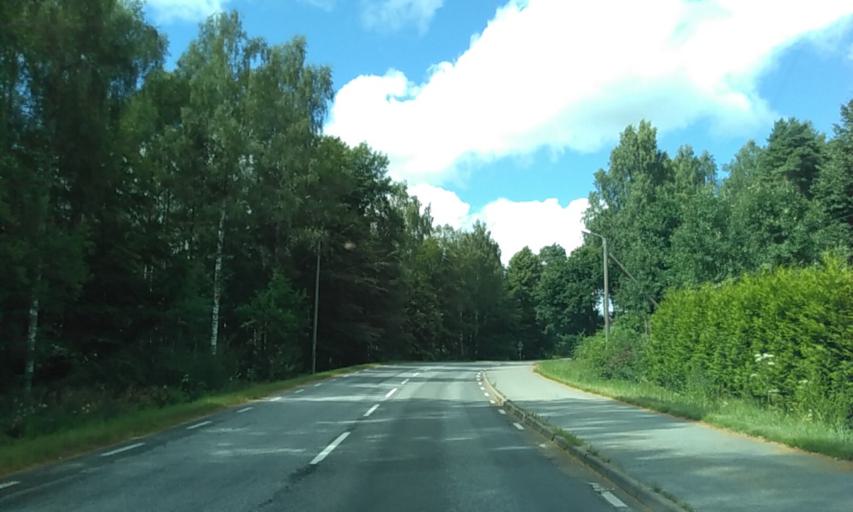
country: SE
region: Vaestra Goetaland
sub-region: Lerums Kommun
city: Grabo
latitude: 57.9197
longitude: 12.3667
